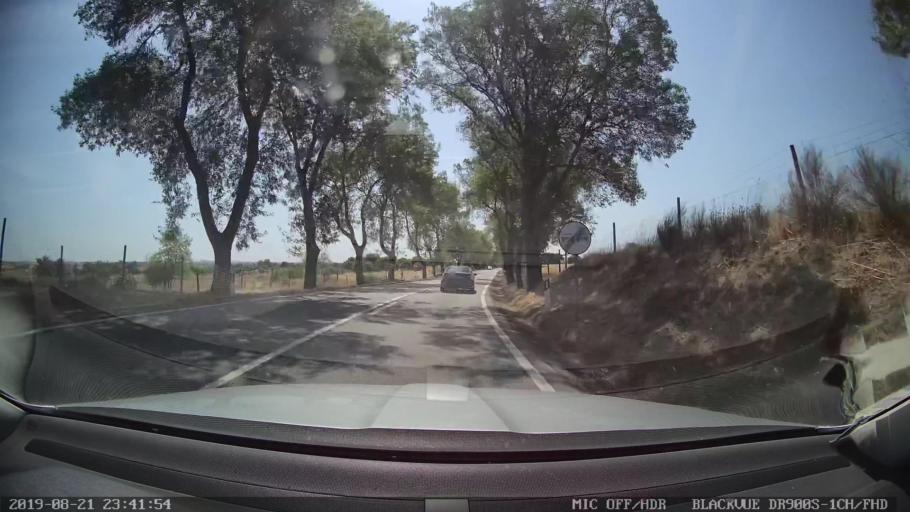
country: PT
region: Castelo Branco
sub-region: Idanha-A-Nova
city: Idanha-a-Nova
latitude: 39.8614
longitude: -7.3169
